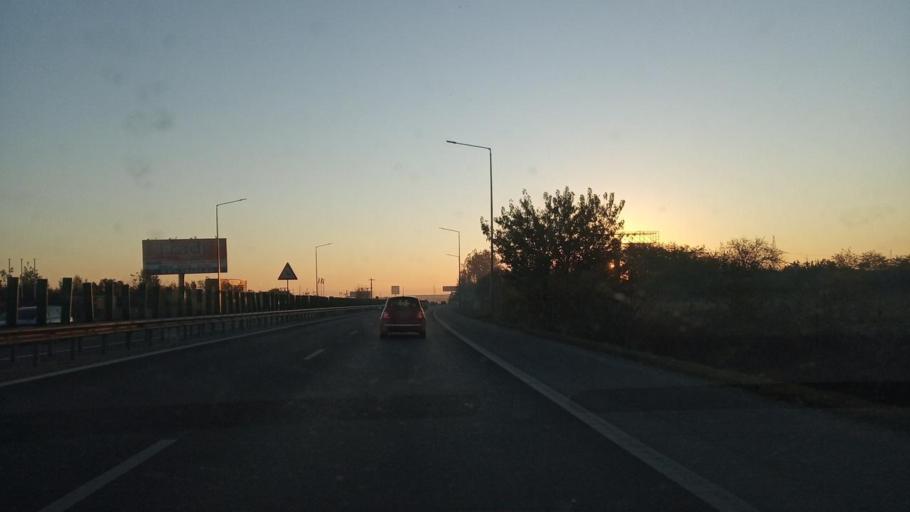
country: RO
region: Ilfov
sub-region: Comuna Glina
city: Catelu
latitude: 44.4080
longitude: 26.2215
